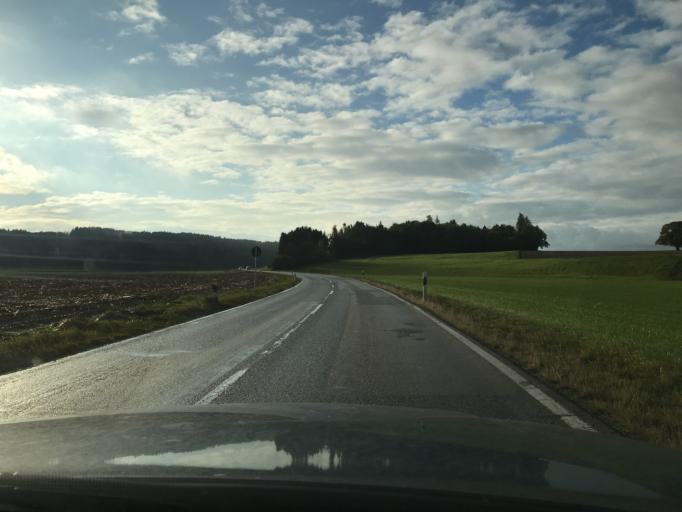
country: DE
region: Bavaria
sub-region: Upper Bavaria
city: Geretsried
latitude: 47.8836
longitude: 11.5059
